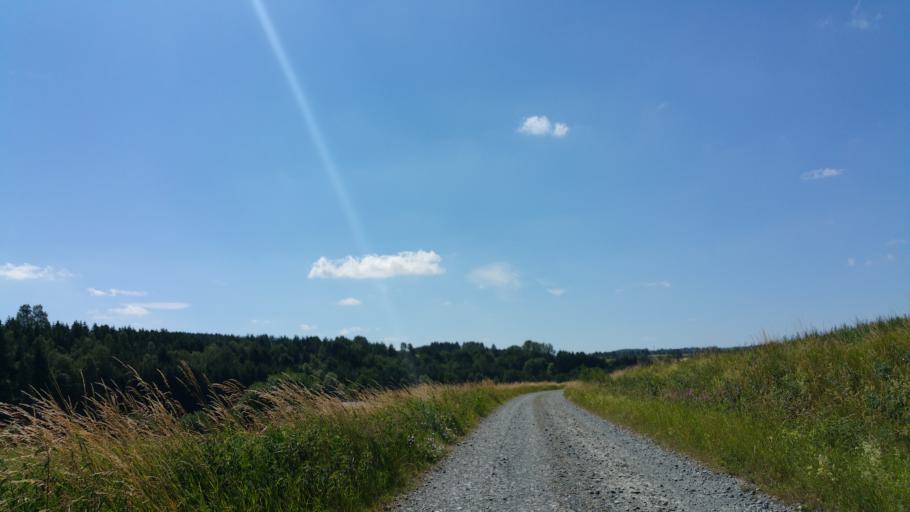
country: DE
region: Bavaria
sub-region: Upper Franconia
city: Topen
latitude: 50.3643
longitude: 11.8509
